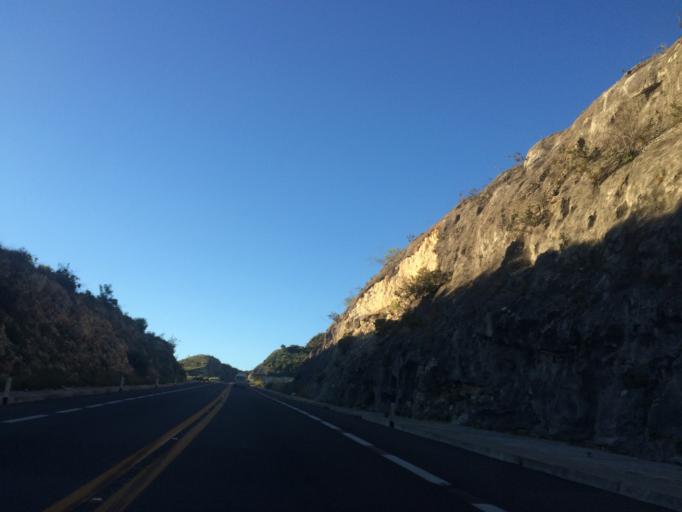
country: MX
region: Puebla
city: Chapuco
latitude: 18.6571
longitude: -97.4559
